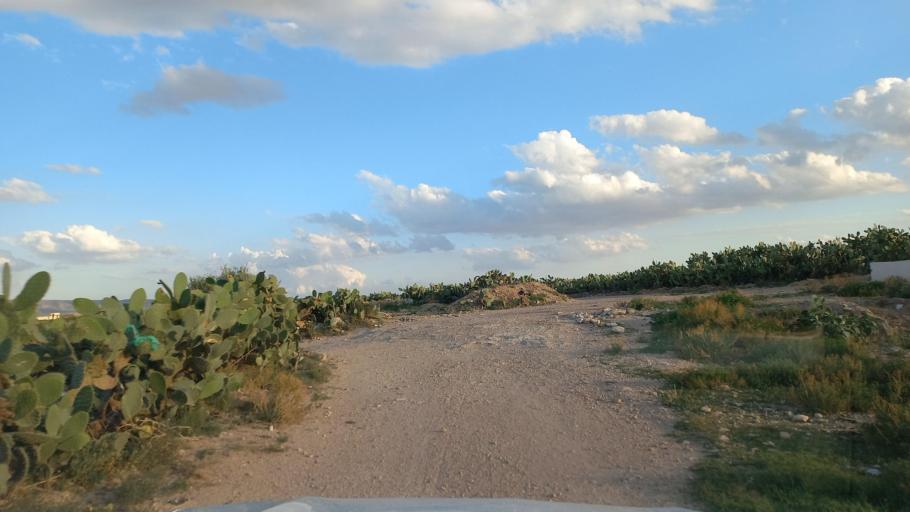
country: TN
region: Al Qasrayn
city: Sbiba
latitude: 35.3779
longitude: 9.0513
